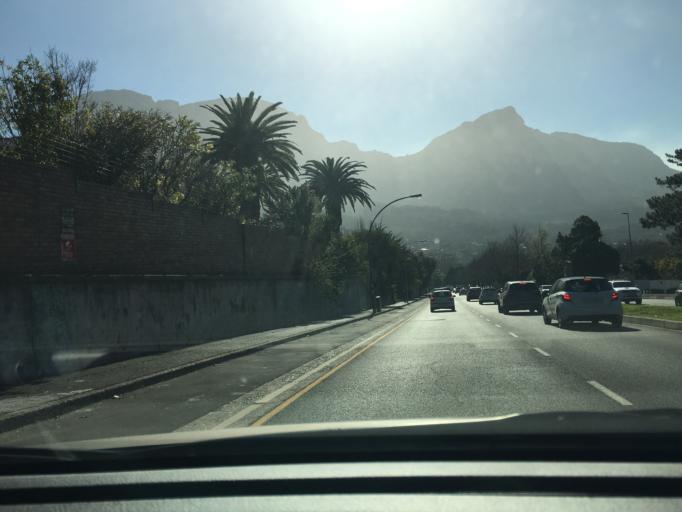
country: ZA
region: Western Cape
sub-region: City of Cape Town
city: Newlands
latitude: -33.9894
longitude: 18.4530
